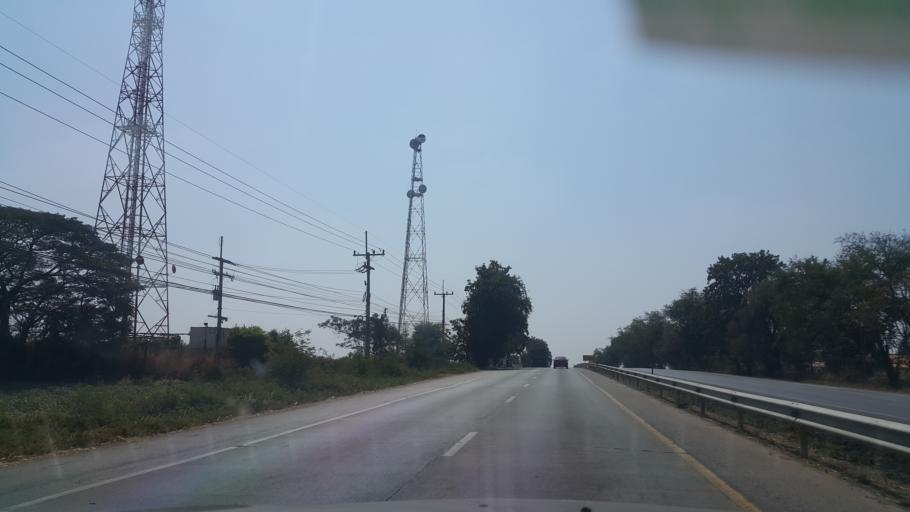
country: TH
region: Khon Kaen
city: Non Sila
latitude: 15.8969
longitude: 102.6494
